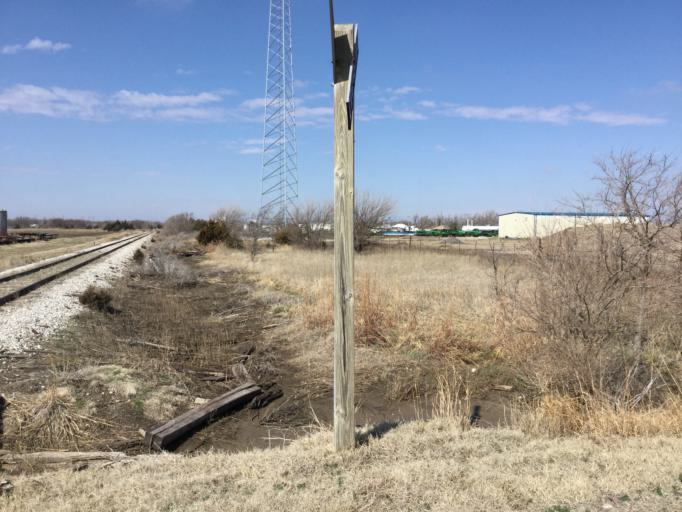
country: US
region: Kansas
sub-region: Barton County
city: Ellinwood
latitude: 38.3523
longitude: -98.5632
